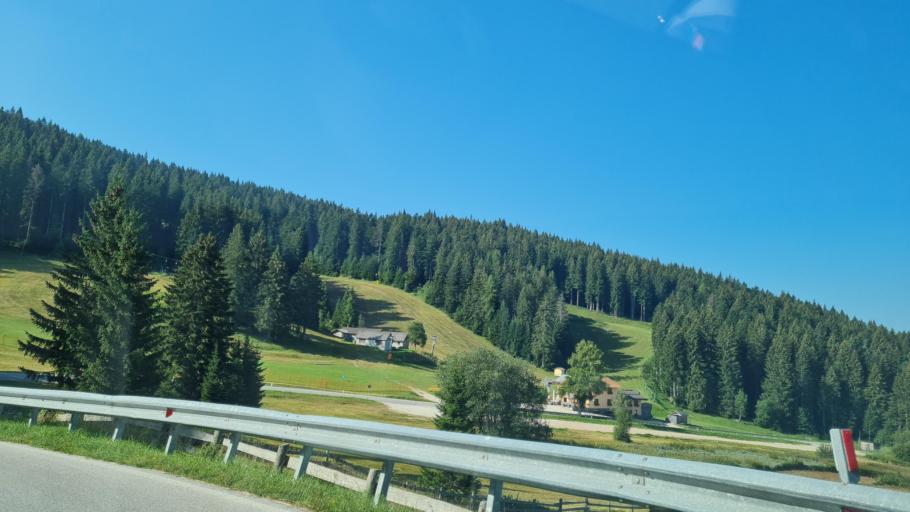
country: IT
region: Trentino-Alto Adige
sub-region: Provincia di Trento
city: Luserna
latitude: 45.9611
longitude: 11.3147
